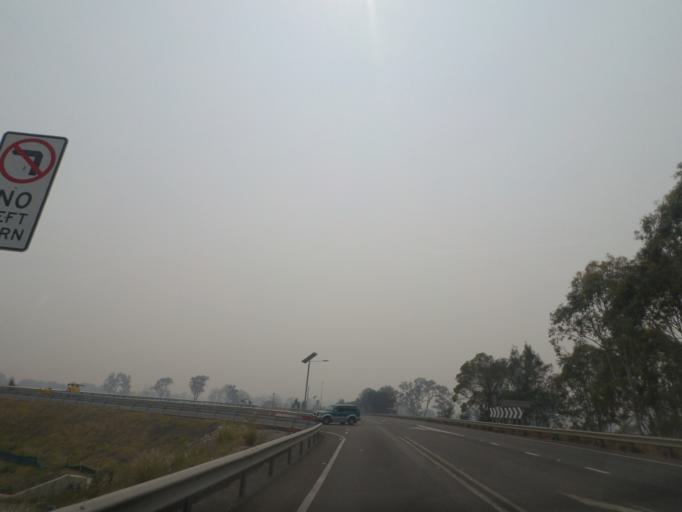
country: AU
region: New South Wales
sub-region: Clarence Valley
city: South Grafton
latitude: -29.7065
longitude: 152.9455
